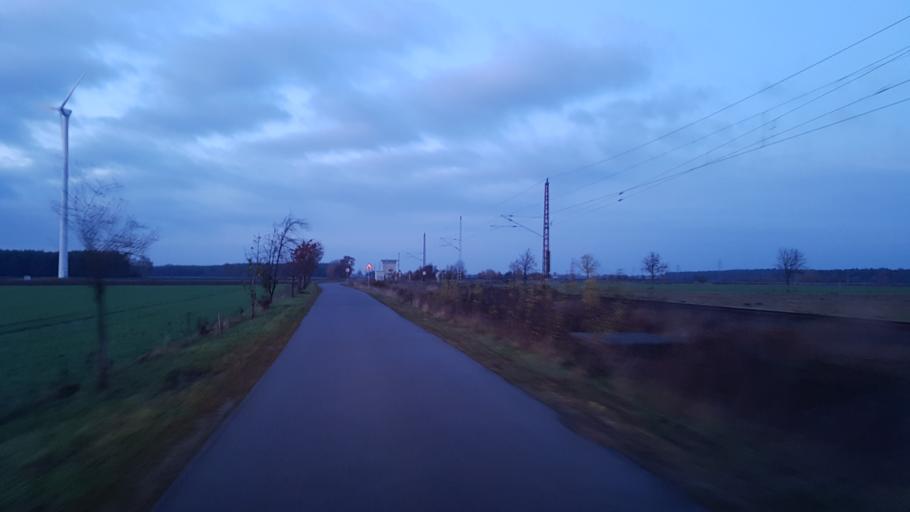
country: DE
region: Brandenburg
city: Falkenberg
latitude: 51.6325
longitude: 13.2248
